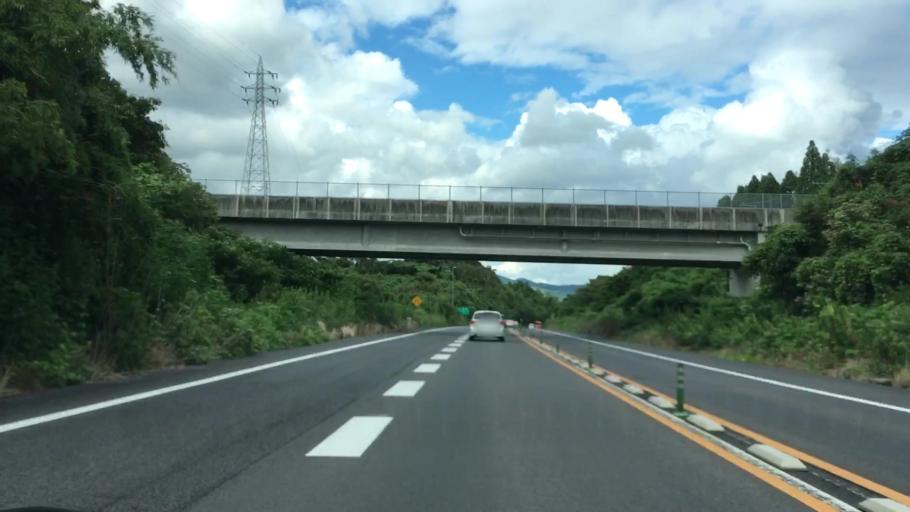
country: JP
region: Saga Prefecture
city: Karatsu
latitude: 33.4229
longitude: 130.0339
